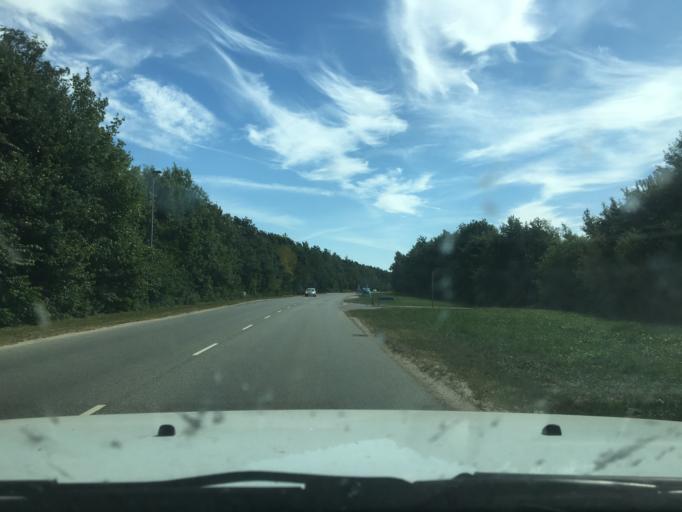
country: DK
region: Central Jutland
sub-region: Viborg Kommune
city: Viborg
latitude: 56.4666
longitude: 9.4471
